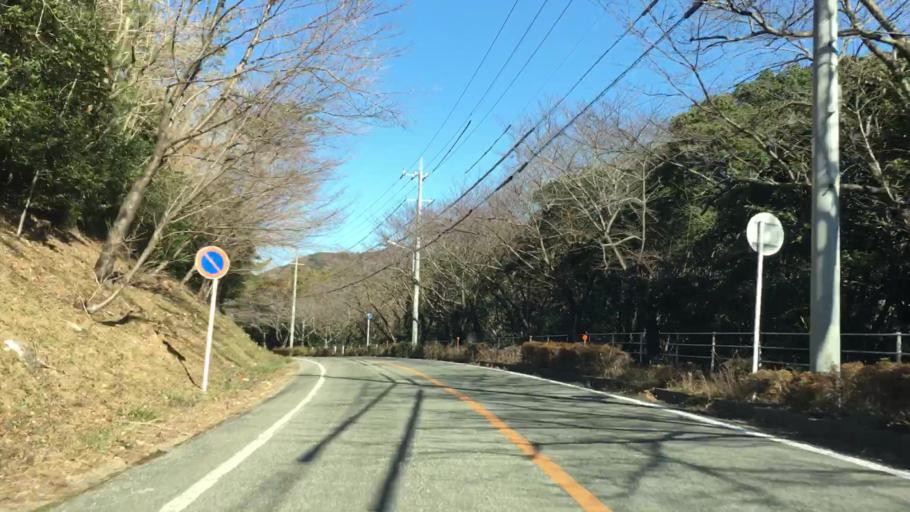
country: JP
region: Aichi
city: Tahara
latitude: 34.6738
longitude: 137.2487
